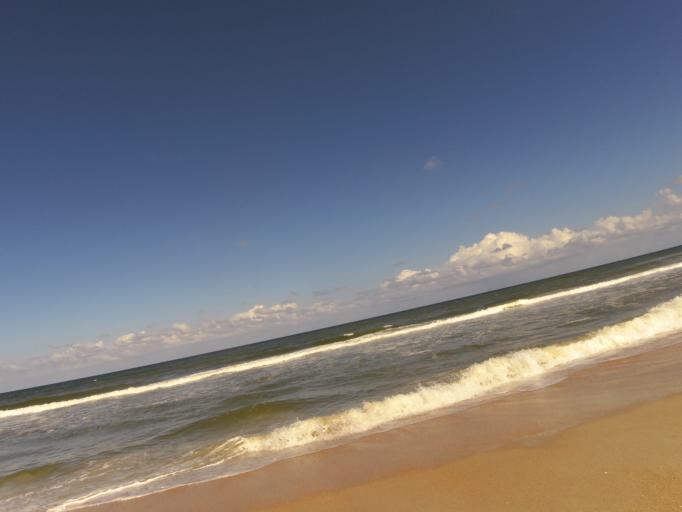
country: US
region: Florida
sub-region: Saint Johns County
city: Palm Valley
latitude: 30.0700
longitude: -81.3333
